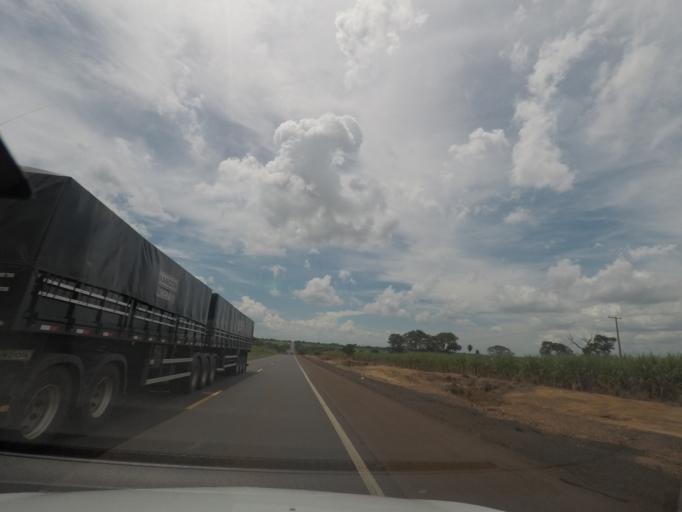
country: BR
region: Sao Paulo
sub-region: Barretos
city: Barretos
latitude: -20.3753
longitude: -48.6442
